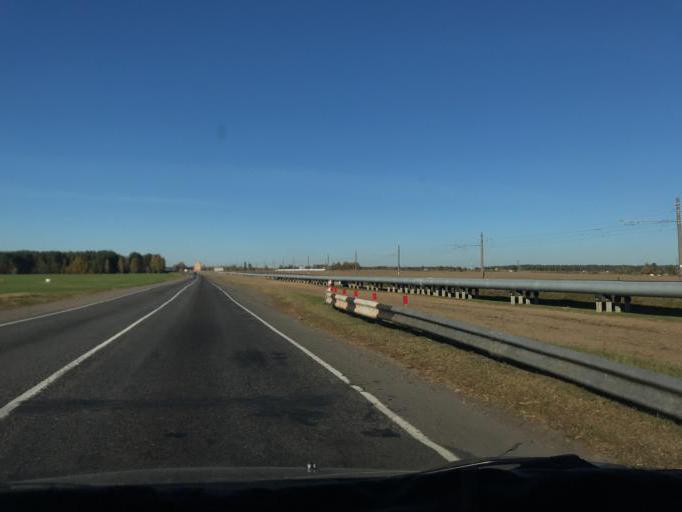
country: BY
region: Gomel
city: Mazyr
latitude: 51.9886
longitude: 29.2593
